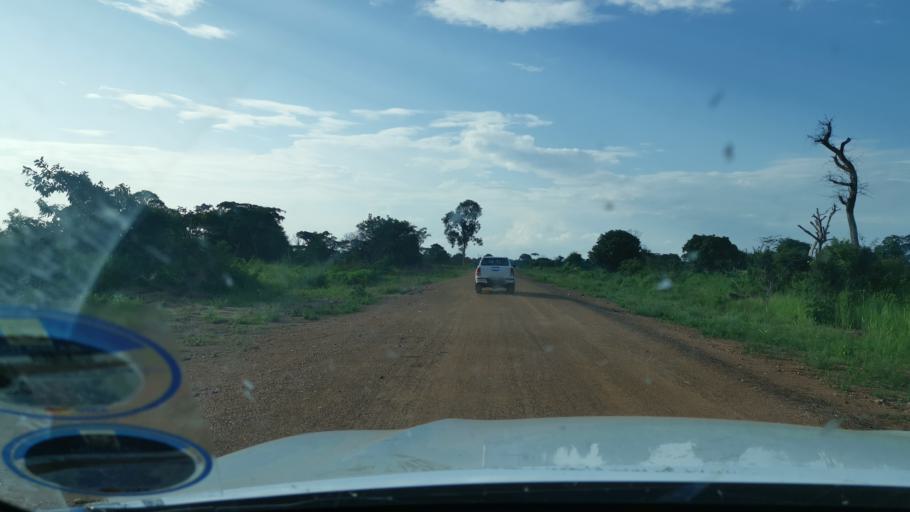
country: ZM
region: Luapula
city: Samfya
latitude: -11.1175
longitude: 29.5791
